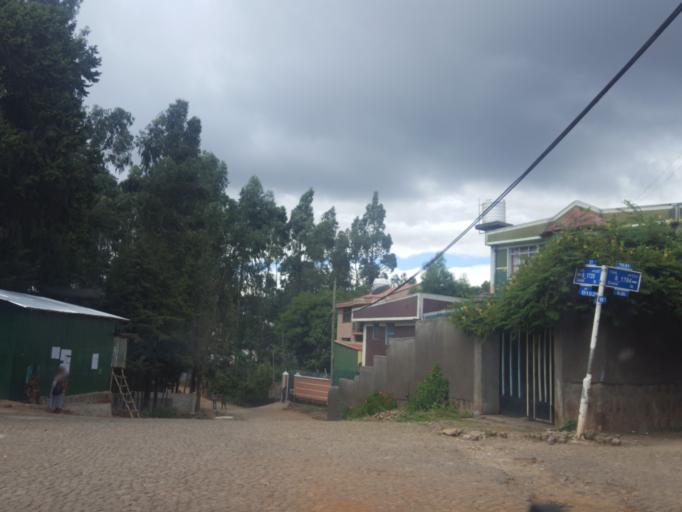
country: ET
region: Adis Abeba
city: Addis Ababa
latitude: 9.0664
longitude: 38.7296
